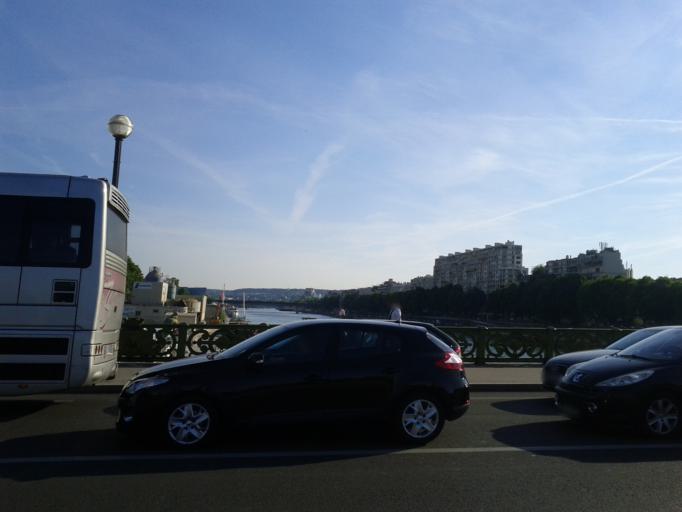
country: FR
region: Ile-de-France
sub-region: Departement des Hauts-de-Seine
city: Issy-les-Moulineaux
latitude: 48.8465
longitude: 2.2762
